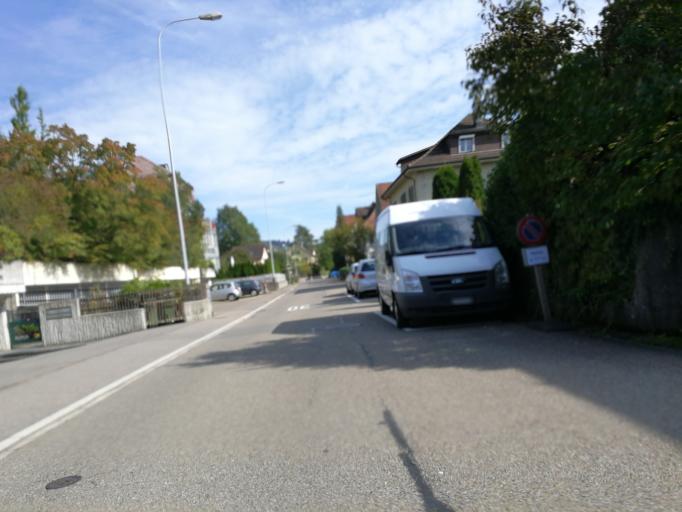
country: CH
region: Zurich
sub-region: Bezirk Meilen
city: Uetikon
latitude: 47.2584
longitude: 8.6834
